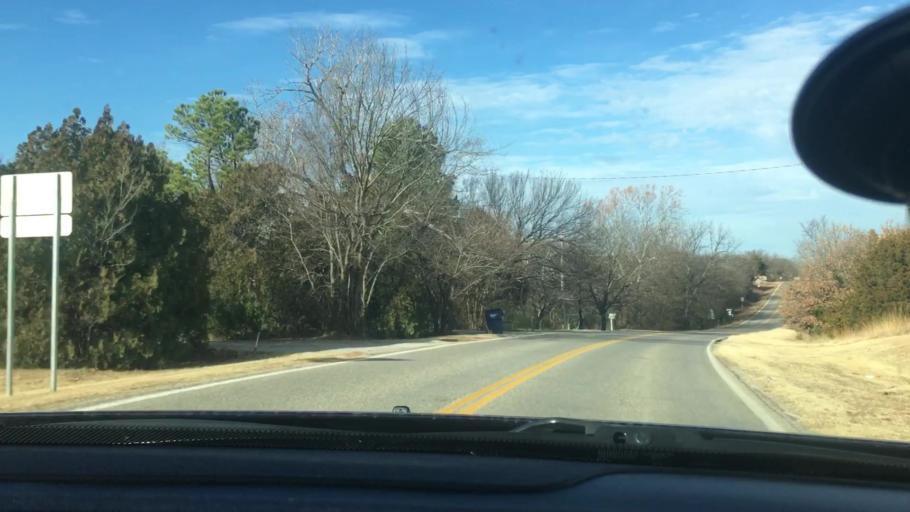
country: US
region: Oklahoma
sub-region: Seminole County
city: Konawa
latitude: 34.9605
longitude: -96.7606
